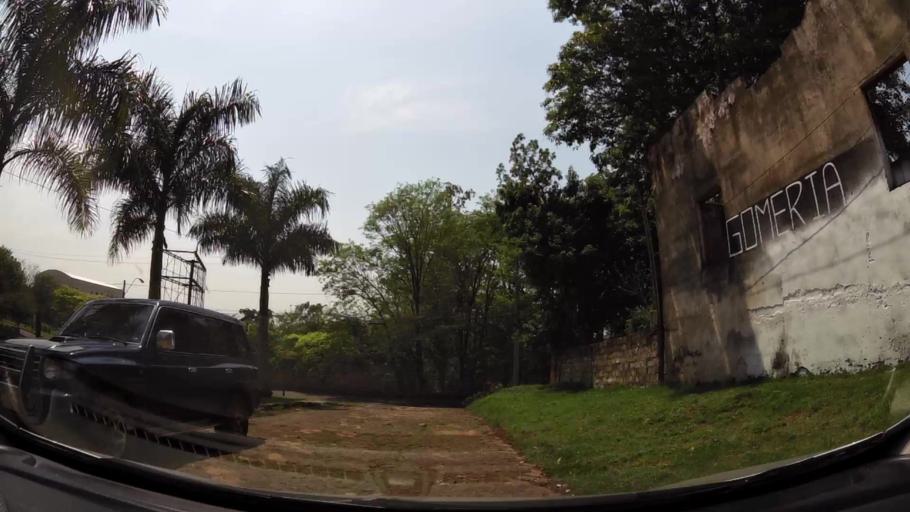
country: PY
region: Alto Parana
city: Presidente Franco
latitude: -25.5247
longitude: -54.6071
